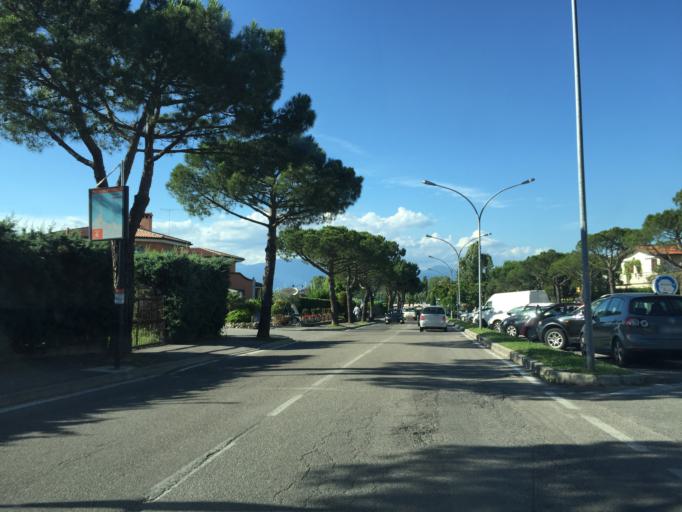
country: IT
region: Lombardy
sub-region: Provincia di Brescia
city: Sirmione
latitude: 45.4698
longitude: 10.6044
